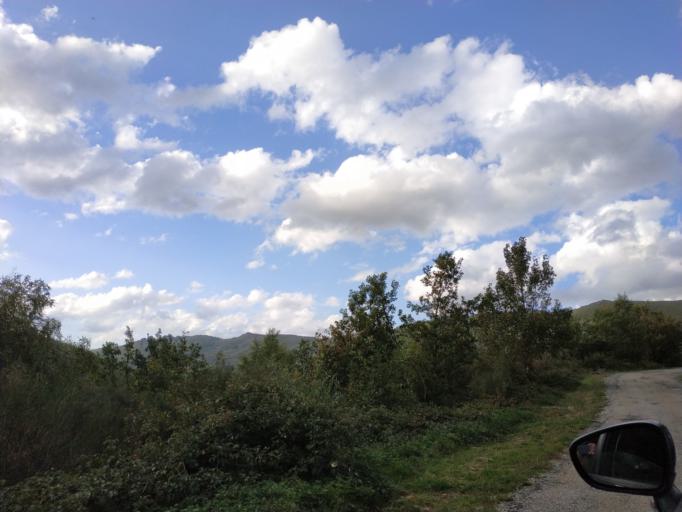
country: ES
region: Castille and Leon
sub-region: Provincia de Leon
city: Candin
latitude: 42.8608
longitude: -6.8538
